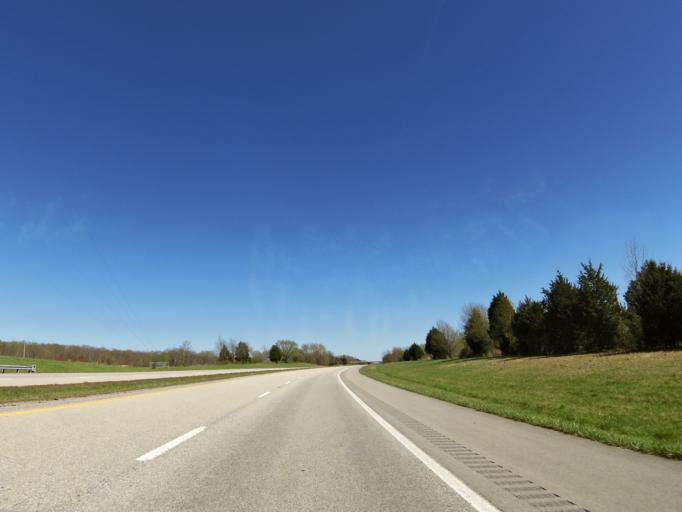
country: US
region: Kentucky
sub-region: Russell County
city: Russell Springs
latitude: 37.0881
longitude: -84.9144
